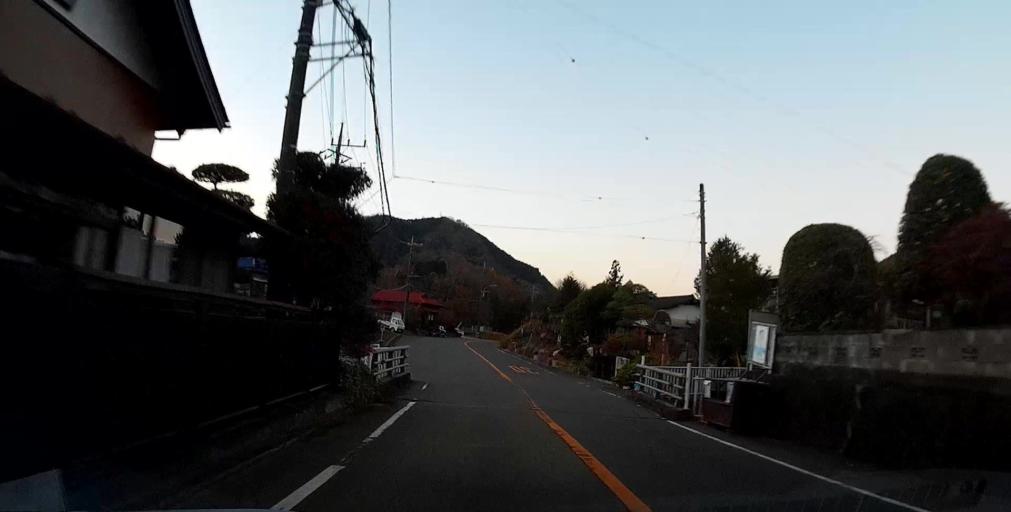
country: JP
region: Yamanashi
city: Uenohara
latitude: 35.5897
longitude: 139.1730
